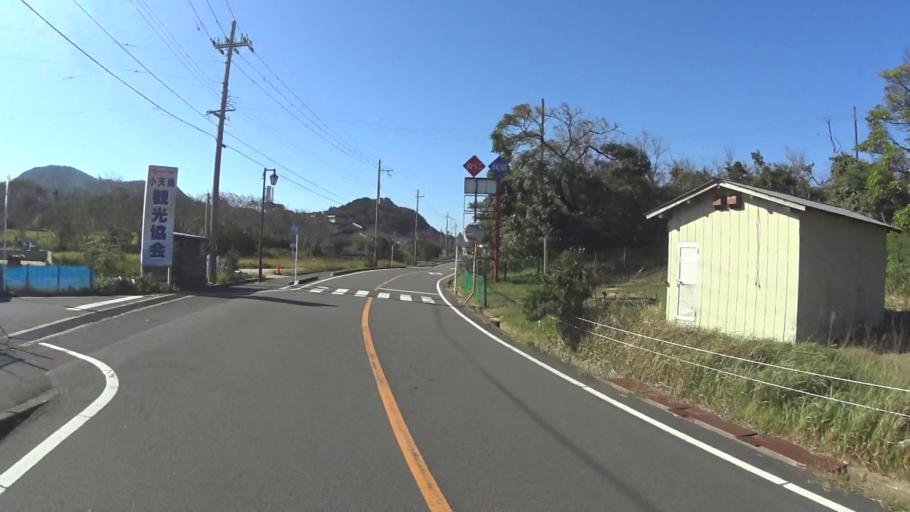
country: JP
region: Hyogo
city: Toyooka
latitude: 35.6438
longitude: 134.9076
